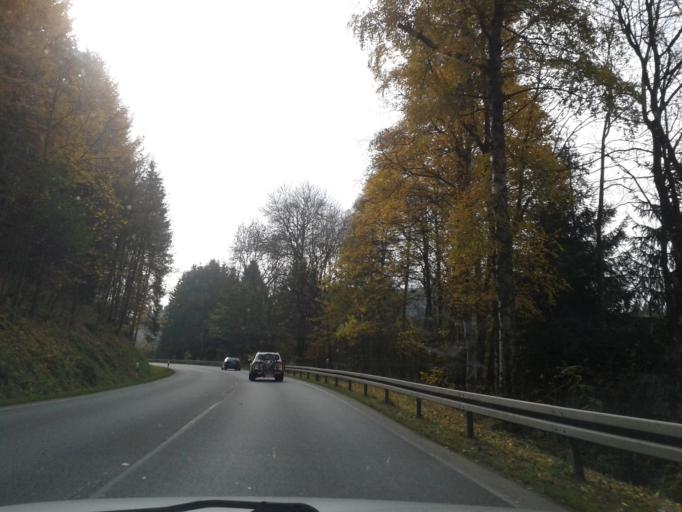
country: DE
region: North Rhine-Westphalia
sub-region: Regierungsbezirk Arnsberg
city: Winterberg
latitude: 51.2516
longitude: 8.5297
